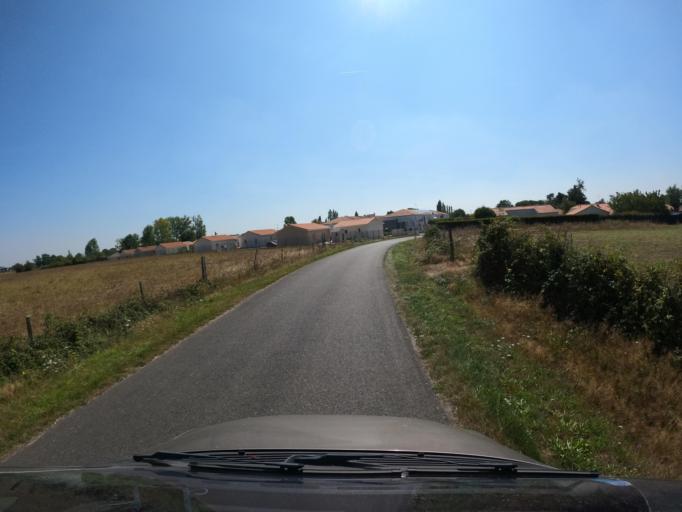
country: FR
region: Pays de la Loire
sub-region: Departement de la Loire-Atlantique
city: La Planche
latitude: 47.0194
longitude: -1.4315
